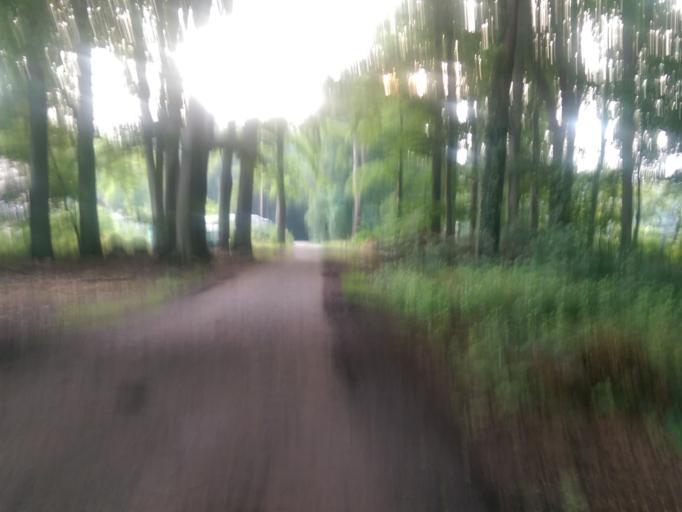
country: DE
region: North Rhine-Westphalia
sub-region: Regierungsbezirk Detmold
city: Guetersloh
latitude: 51.8703
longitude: 8.3517
